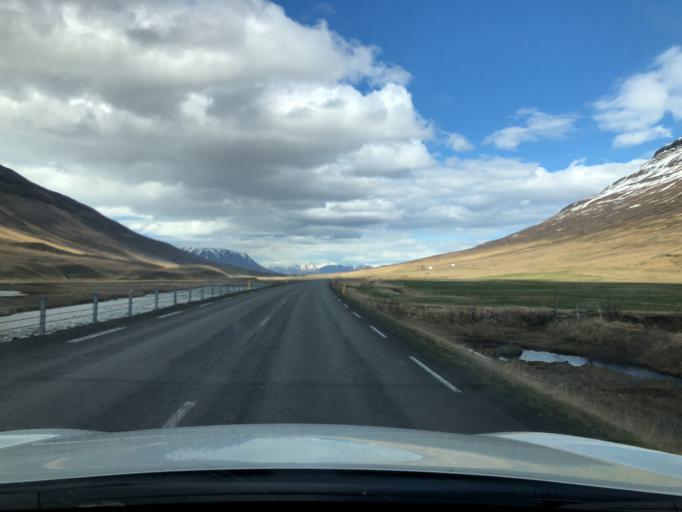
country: IS
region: Northeast
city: Dalvik
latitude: 65.6312
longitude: -18.4796
